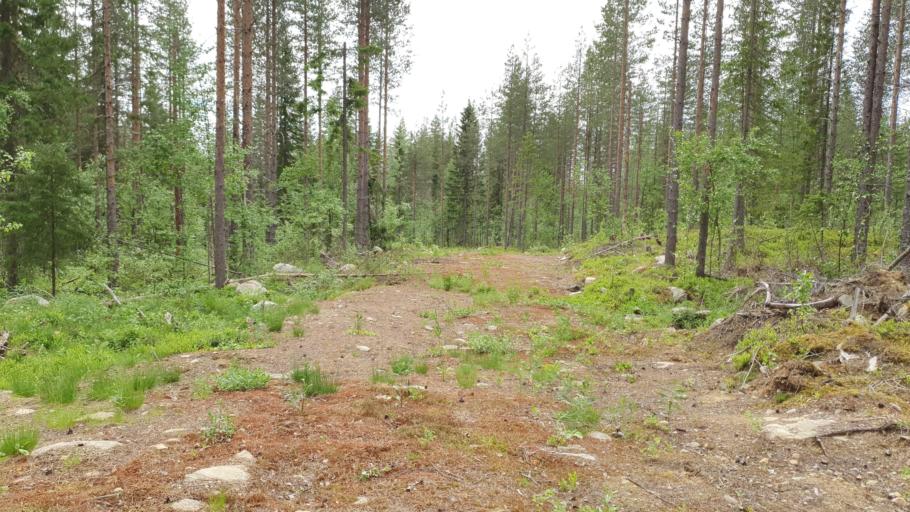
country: FI
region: Kainuu
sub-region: Kehys-Kainuu
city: Kuhmo
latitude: 64.4451
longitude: 29.6835
